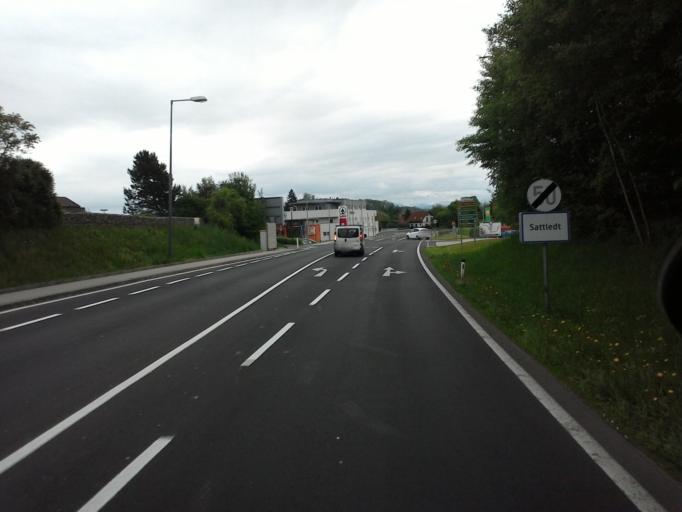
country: AT
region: Upper Austria
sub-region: Wels-Land
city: Sattledt
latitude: 48.0727
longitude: 14.0521
